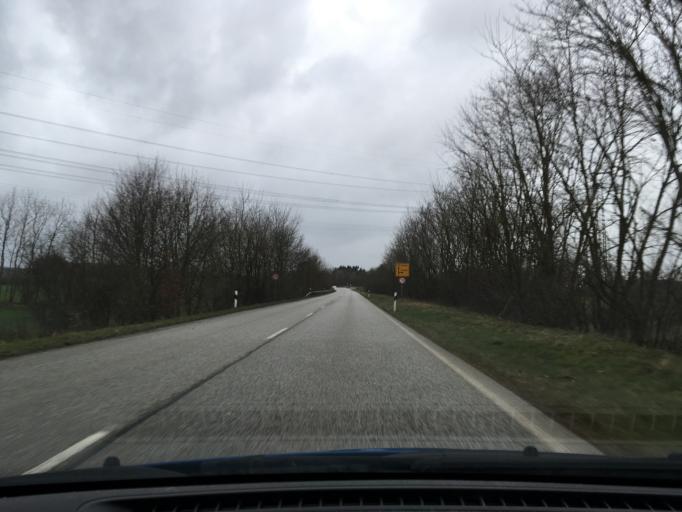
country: DE
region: Schleswig-Holstein
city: Grabau
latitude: 53.4878
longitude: 10.5214
